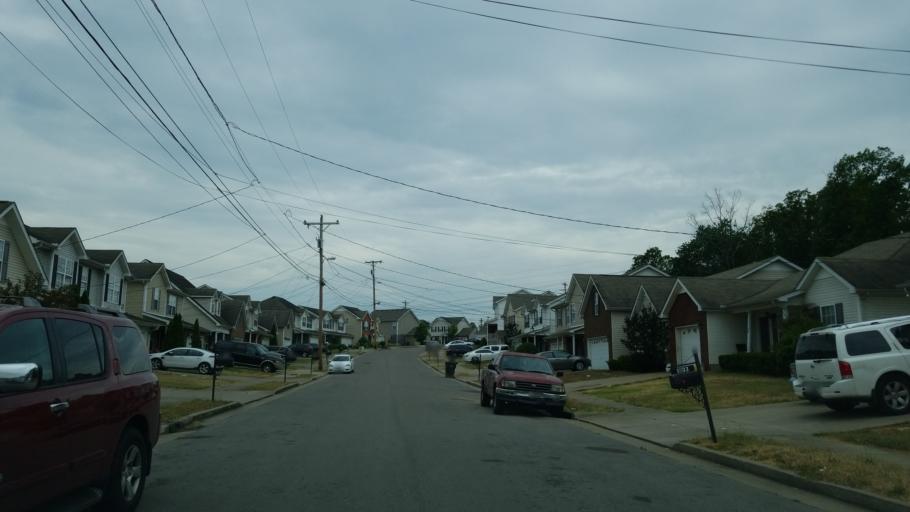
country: US
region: Tennessee
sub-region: Rutherford County
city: La Vergne
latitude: 36.0541
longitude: -86.5961
